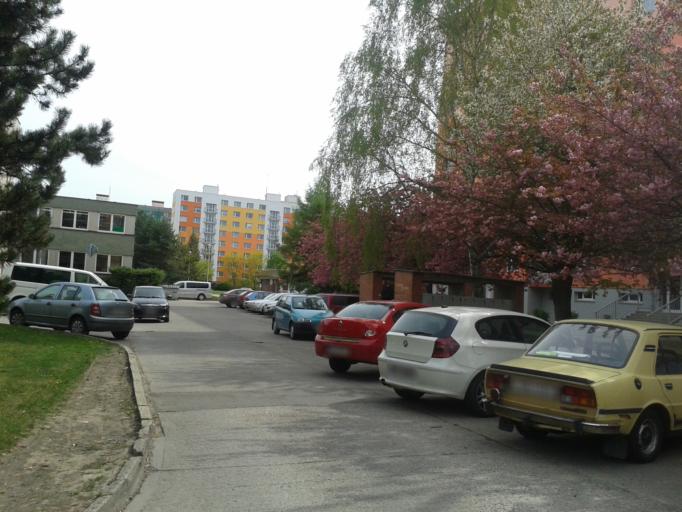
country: CZ
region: Pardubicky
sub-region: Okres Pardubice
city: Pardubice
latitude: 50.0438
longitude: 15.8074
